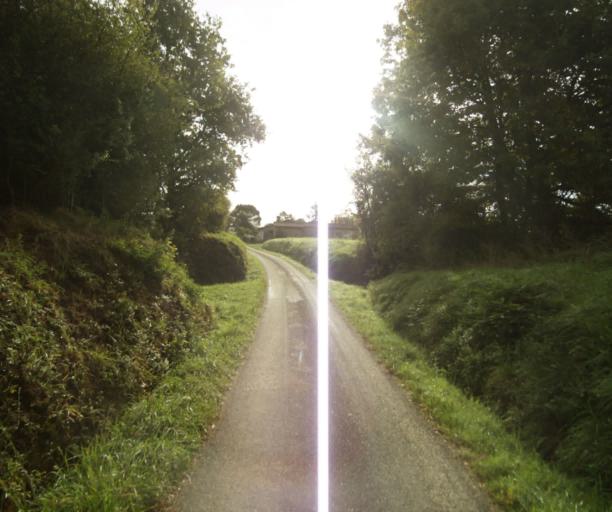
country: FR
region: Midi-Pyrenees
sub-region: Departement du Gers
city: Nogaro
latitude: 43.8199
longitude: -0.0727
